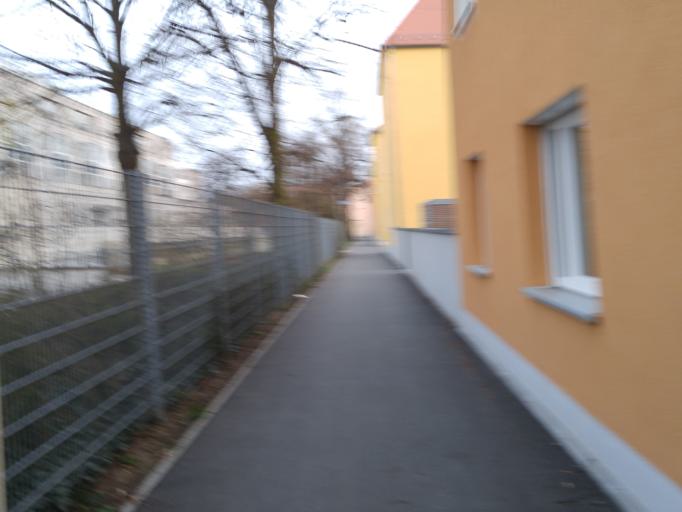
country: DE
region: Bavaria
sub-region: Regierungsbezirk Mittelfranken
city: Nuernberg
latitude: 49.4697
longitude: 11.1112
